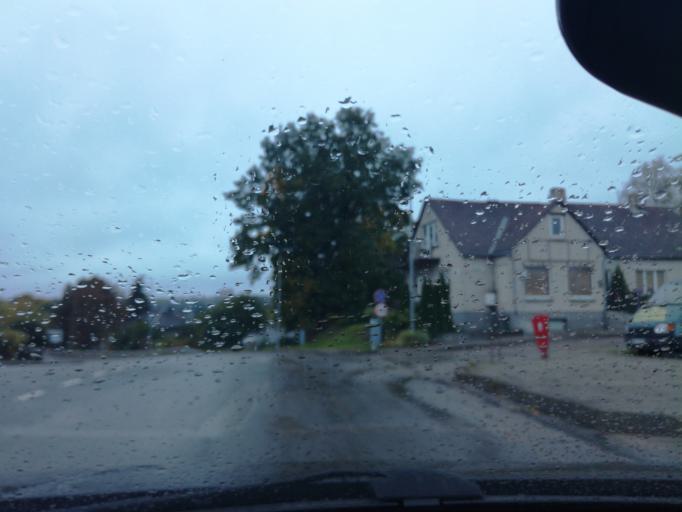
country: LT
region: Alytaus apskritis
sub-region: Alytus
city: Alytus
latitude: 54.4031
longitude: 24.0588
